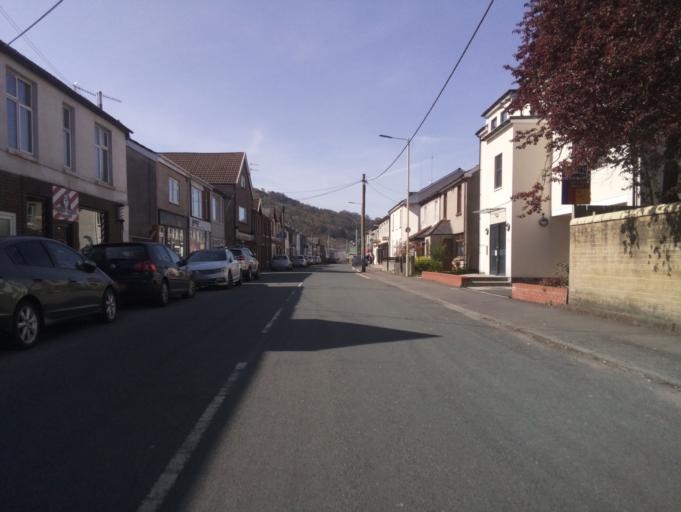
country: GB
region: Wales
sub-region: Cardiff
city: Radyr
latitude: 51.5412
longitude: -3.2660
